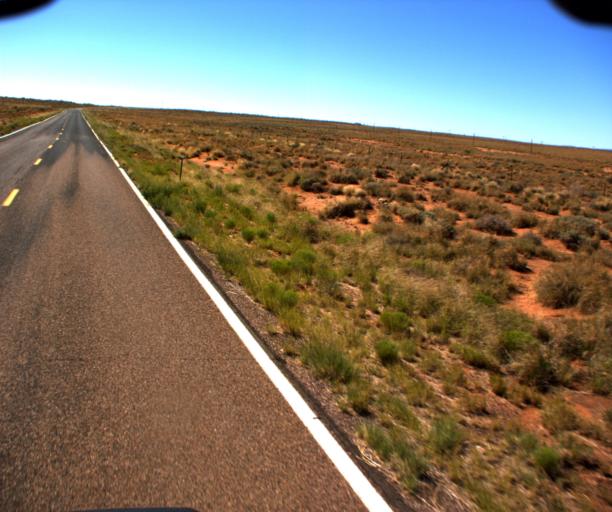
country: US
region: Arizona
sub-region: Coconino County
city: LeChee
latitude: 35.1311
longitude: -110.8802
